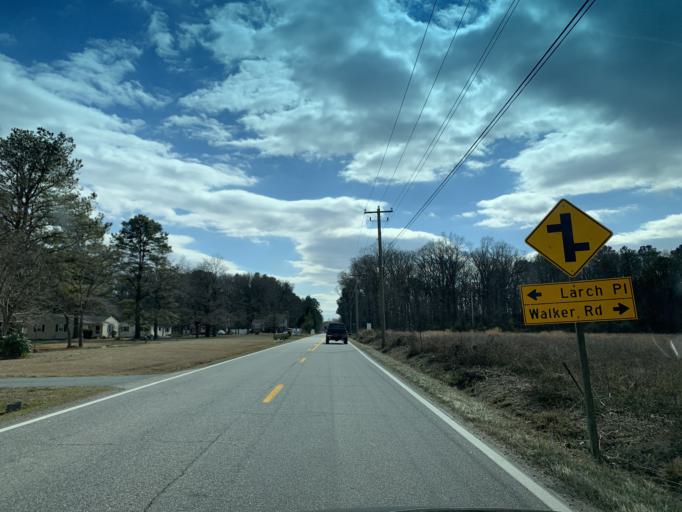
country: US
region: Maryland
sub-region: Queen Anne's County
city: Stevensville
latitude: 38.9970
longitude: -76.3118
